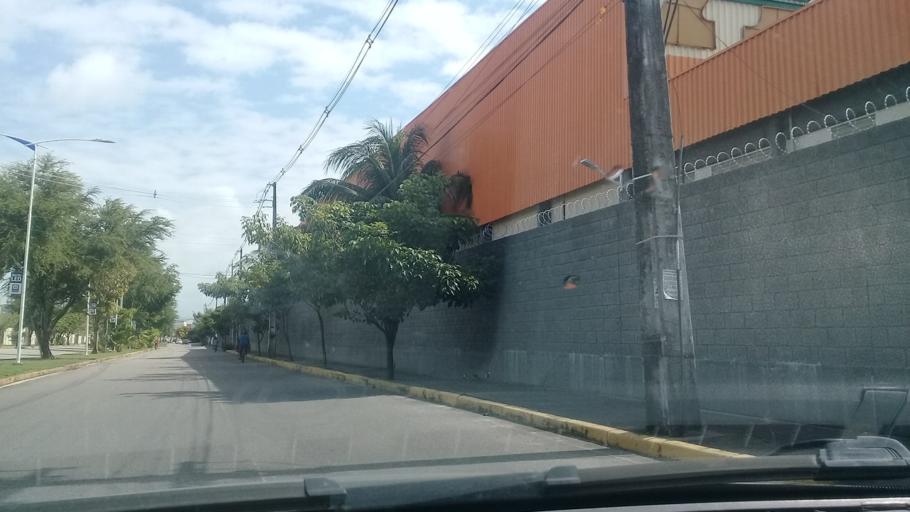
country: BR
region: Pernambuco
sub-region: Jaboatao Dos Guararapes
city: Jaboatao
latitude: -8.1660
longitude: -34.9196
